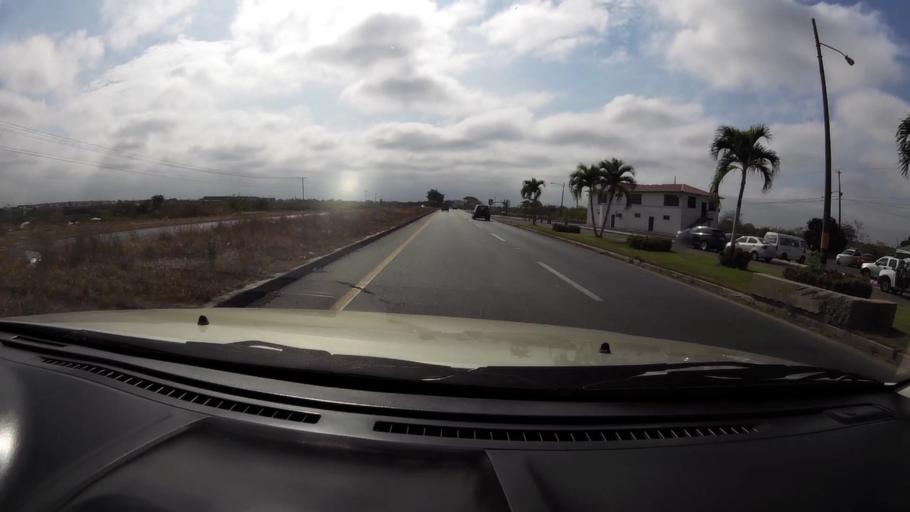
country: EC
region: Guayas
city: Eloy Alfaro
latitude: -2.1943
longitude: -79.7898
